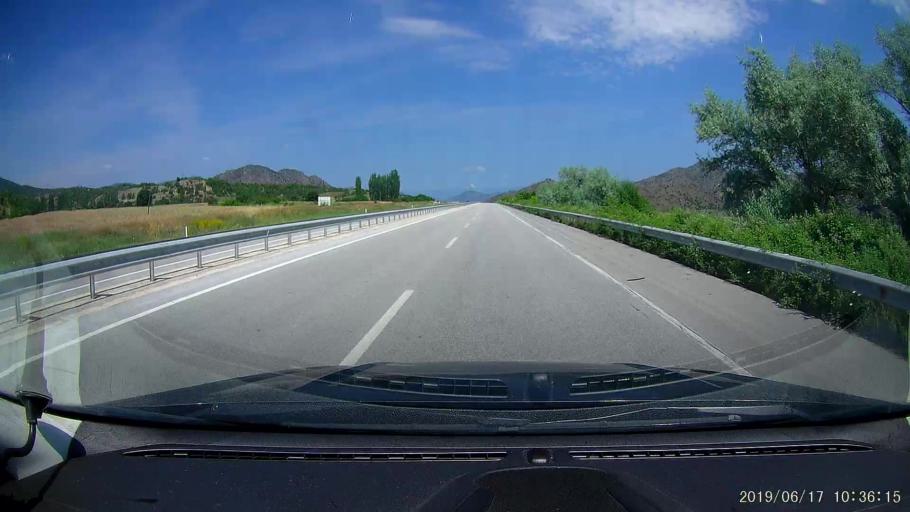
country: TR
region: Corum
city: Osmancik
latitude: 40.9766
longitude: 34.6851
